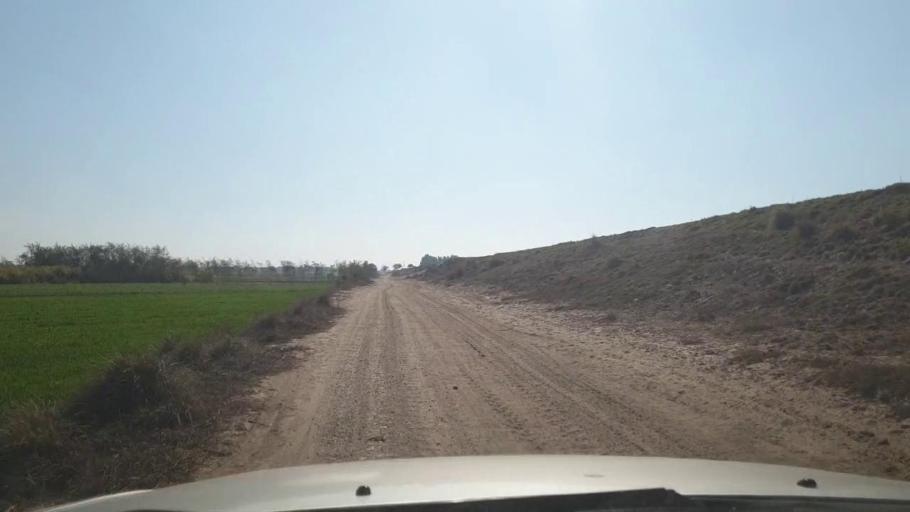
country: PK
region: Sindh
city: Ghotki
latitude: 28.0238
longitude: 69.2099
